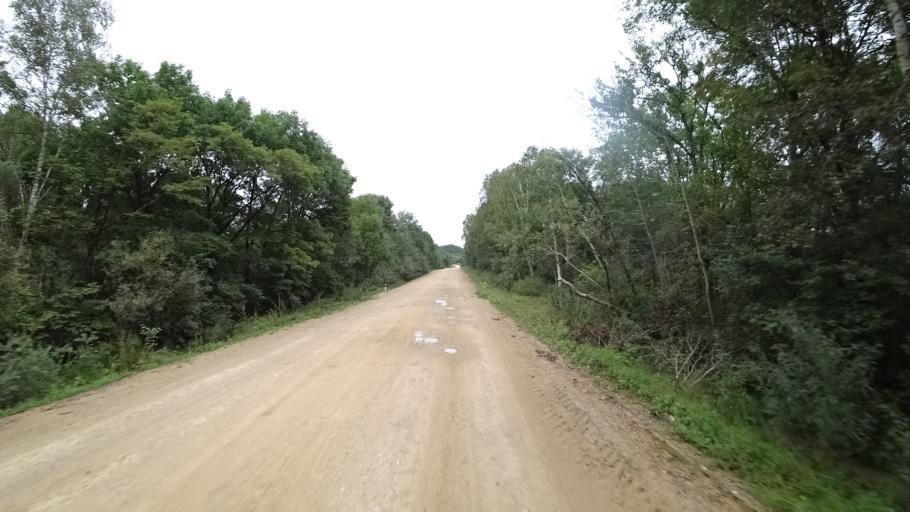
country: RU
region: Primorskiy
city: Rettikhovka
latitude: 44.1629
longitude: 132.7295
